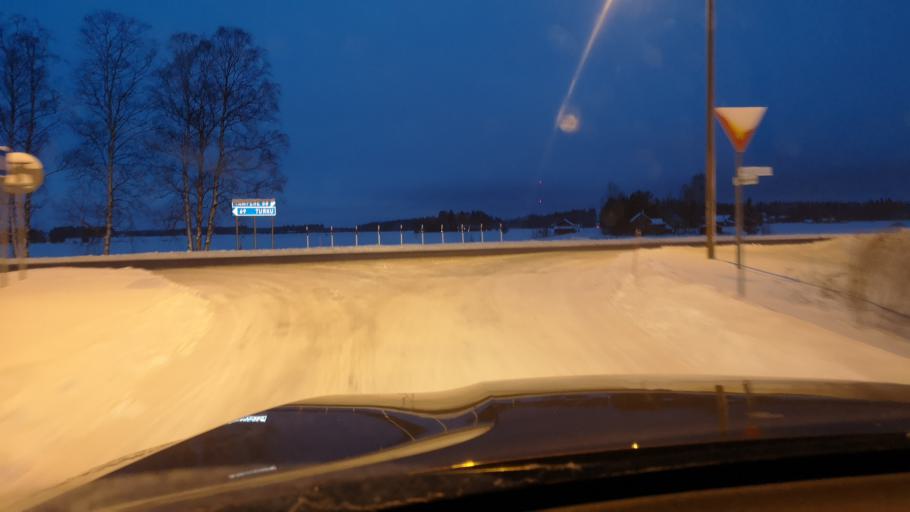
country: FI
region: Varsinais-Suomi
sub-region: Loimaa
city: Loimaa
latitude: 60.8847
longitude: 23.0893
